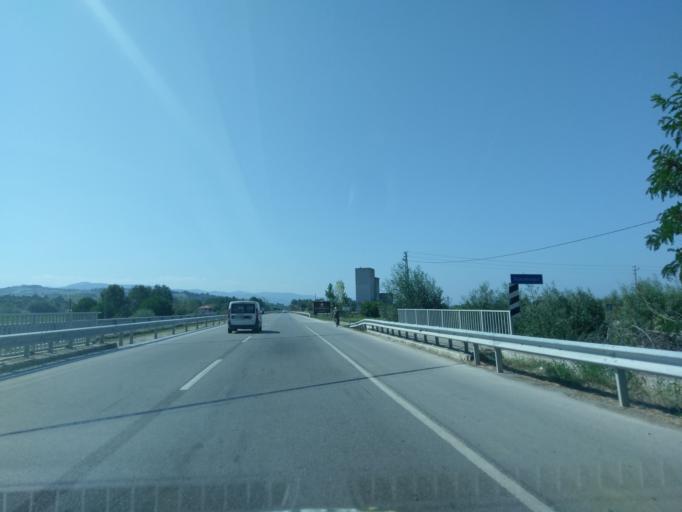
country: TR
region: Samsun
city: Alacam
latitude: 41.6093
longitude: 35.6592
